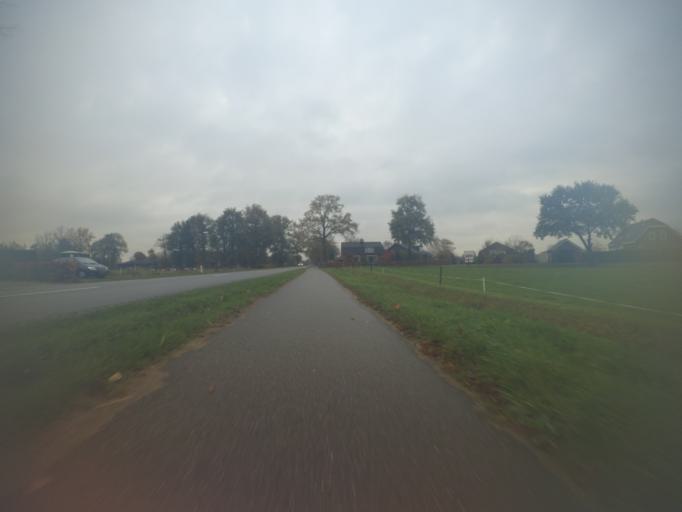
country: NL
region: Gelderland
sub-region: Gemeente Barneveld
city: Barneveld
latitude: 52.1083
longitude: 5.5500
